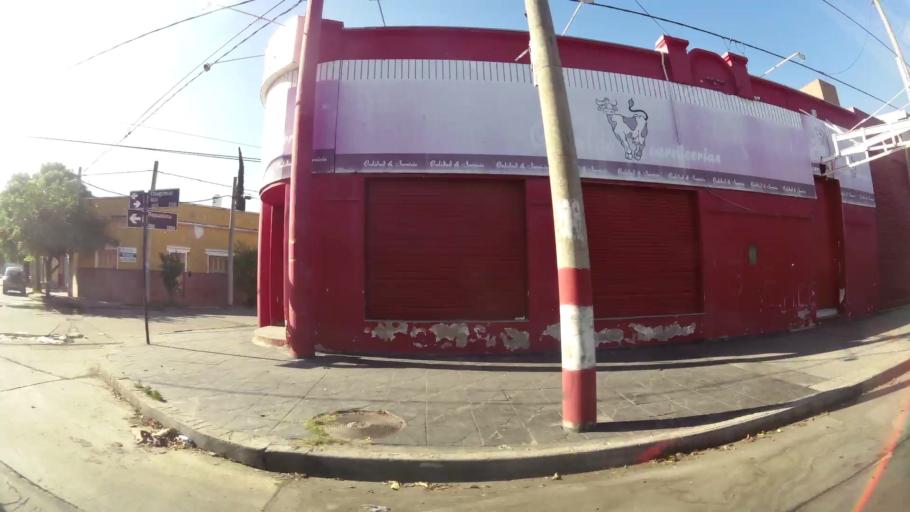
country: AR
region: Cordoba
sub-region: Departamento de Capital
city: Cordoba
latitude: -31.3895
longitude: -64.1743
